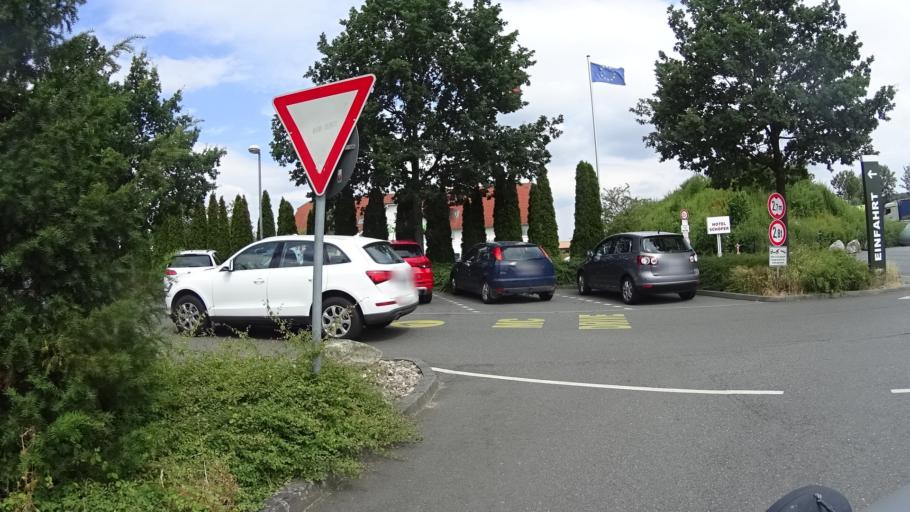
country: DE
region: Lower Saxony
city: Bockenem
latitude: 51.9473
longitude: 10.1387
